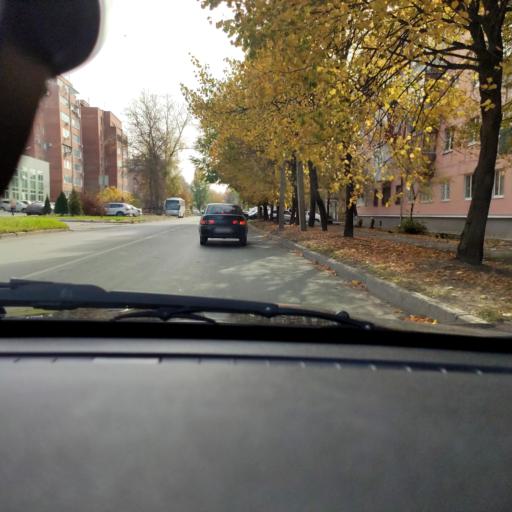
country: RU
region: Samara
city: Tol'yatti
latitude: 53.5090
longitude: 49.4066
